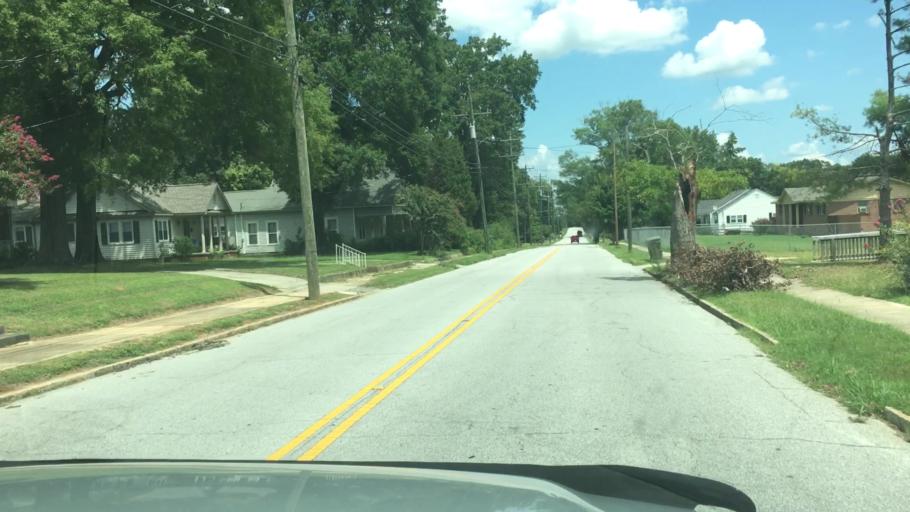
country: US
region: South Carolina
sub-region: Laurens County
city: Clinton
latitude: 34.4745
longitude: -81.8716
